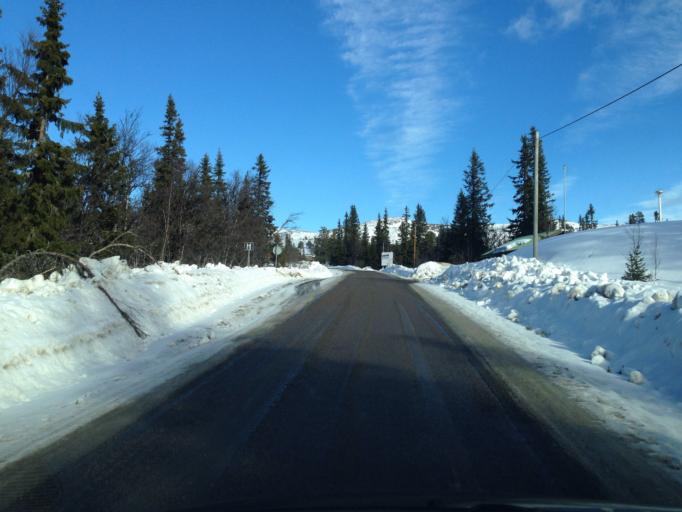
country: SE
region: Jaemtland
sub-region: Harjedalens Kommun
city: Sveg
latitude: 62.1322
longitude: 13.2747
